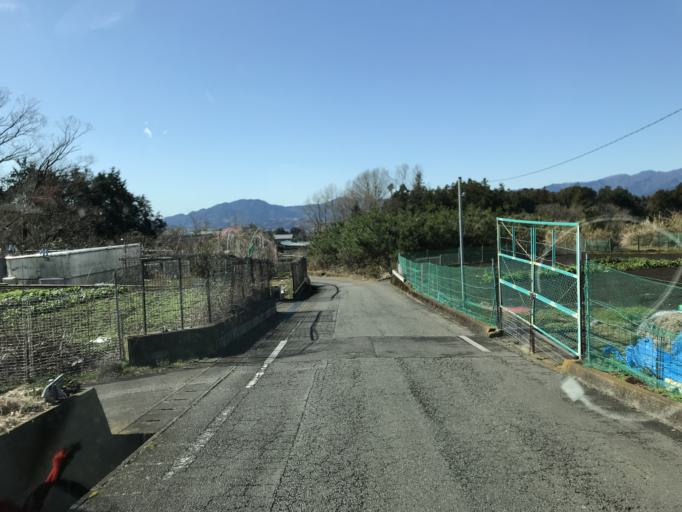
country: JP
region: Shizuoka
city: Fujinomiya
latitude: 35.2420
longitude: 138.6596
